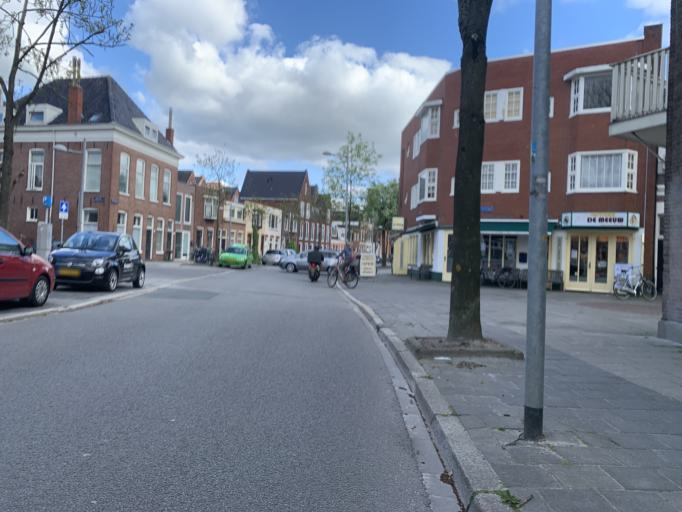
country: NL
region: Groningen
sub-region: Gemeente Groningen
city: Oosterpark
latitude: 53.2105
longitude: 6.5796
